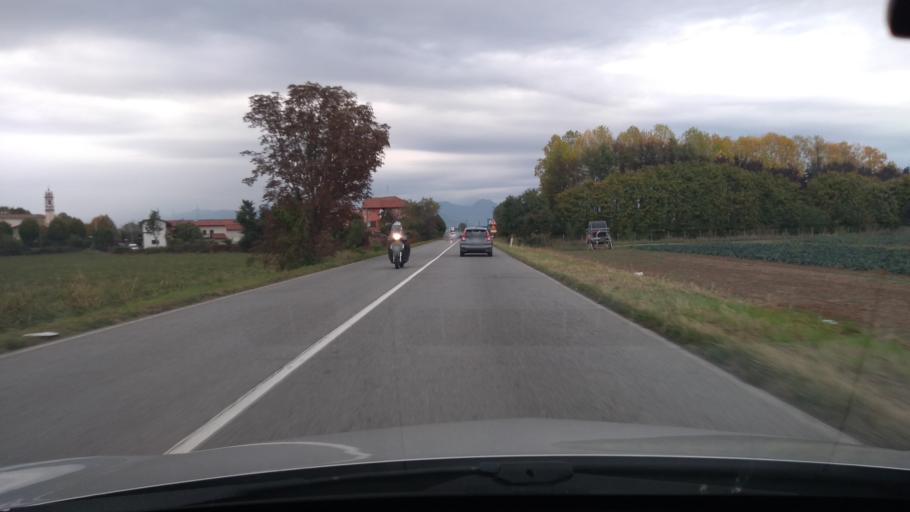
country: IT
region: Lombardy
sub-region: Provincia di Bergamo
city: Levate
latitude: 45.6228
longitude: 9.6367
